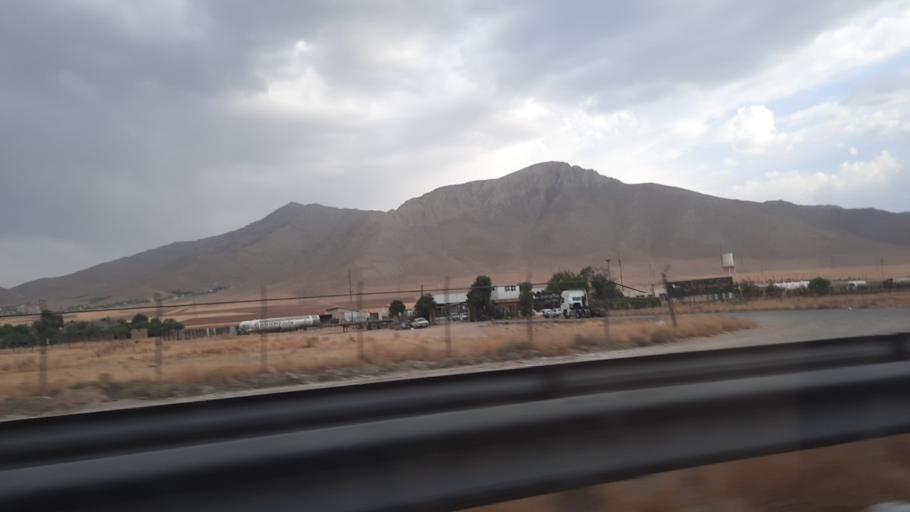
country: IR
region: Markazi
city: Arak
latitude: 34.0172
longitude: 49.5568
